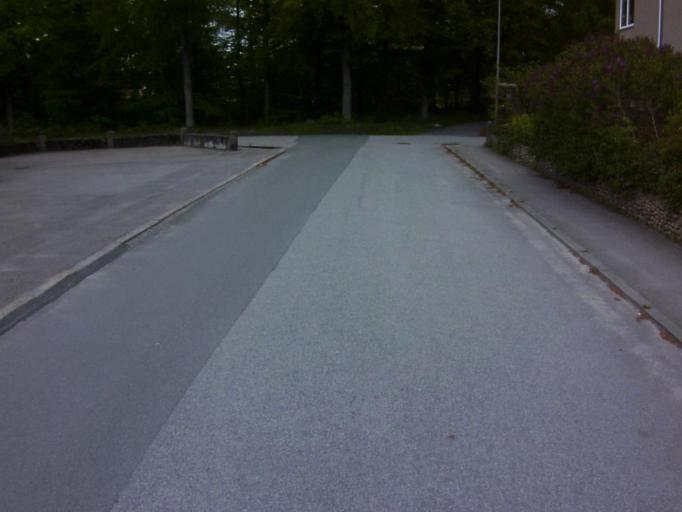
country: SE
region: Blekinge
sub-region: Solvesborgs Kommun
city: Soelvesborg
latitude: 56.0495
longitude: 14.5731
